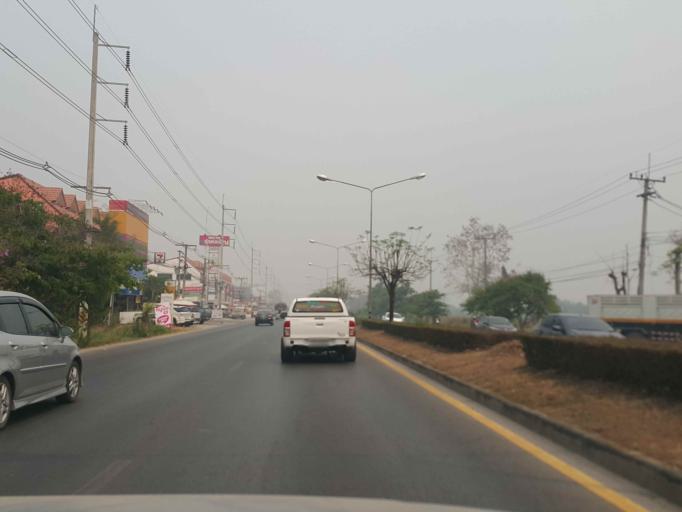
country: TH
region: Chiang Mai
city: San Sai
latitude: 18.8605
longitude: 99.0147
